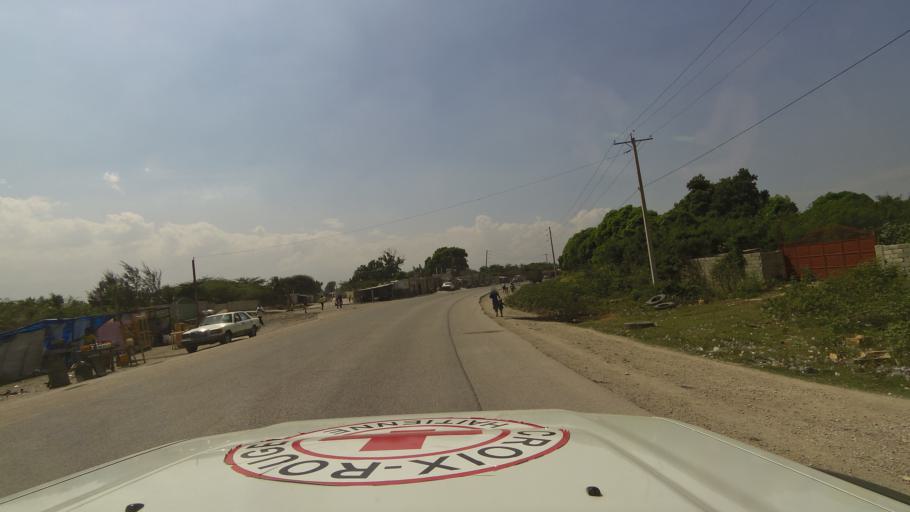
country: HT
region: Ouest
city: Croix des Bouquets
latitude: 18.6380
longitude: -72.2642
